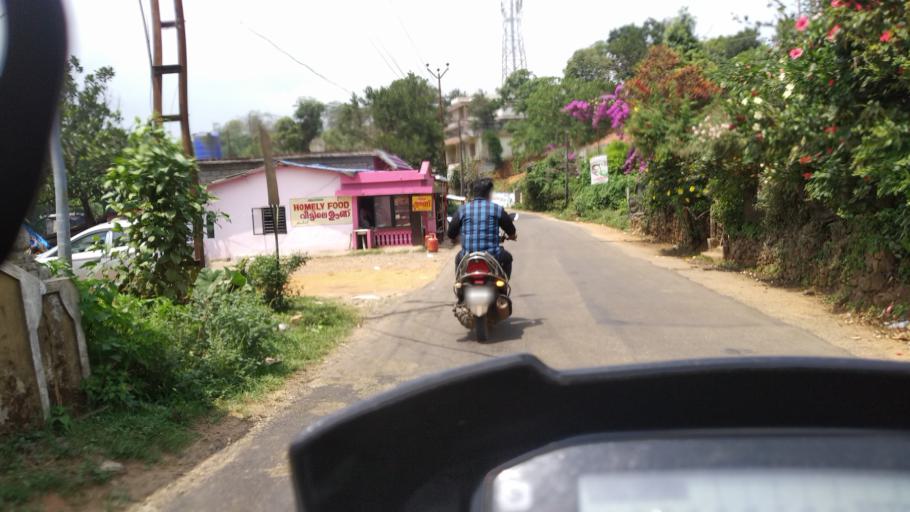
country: IN
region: Kerala
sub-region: Kottayam
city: Erattupetta
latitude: 9.6554
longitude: 76.9260
